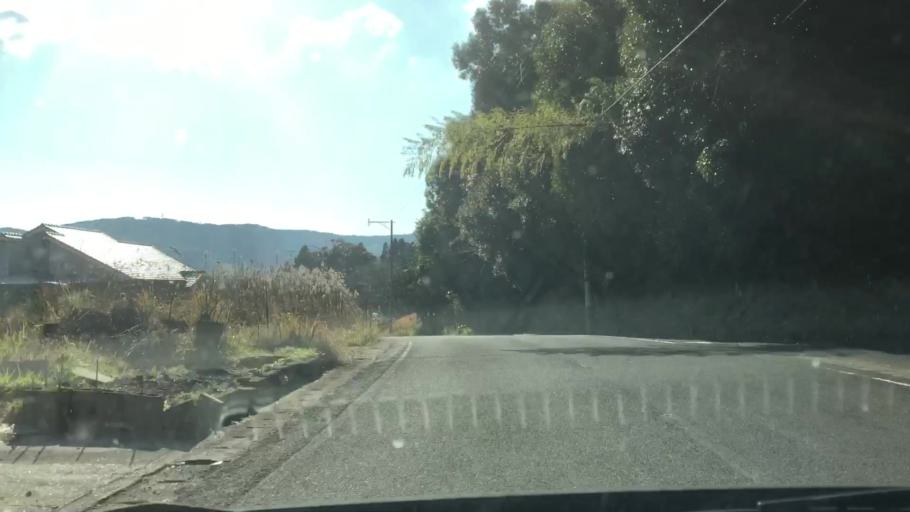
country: JP
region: Kagoshima
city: Satsumasendai
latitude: 31.8581
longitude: 130.3652
